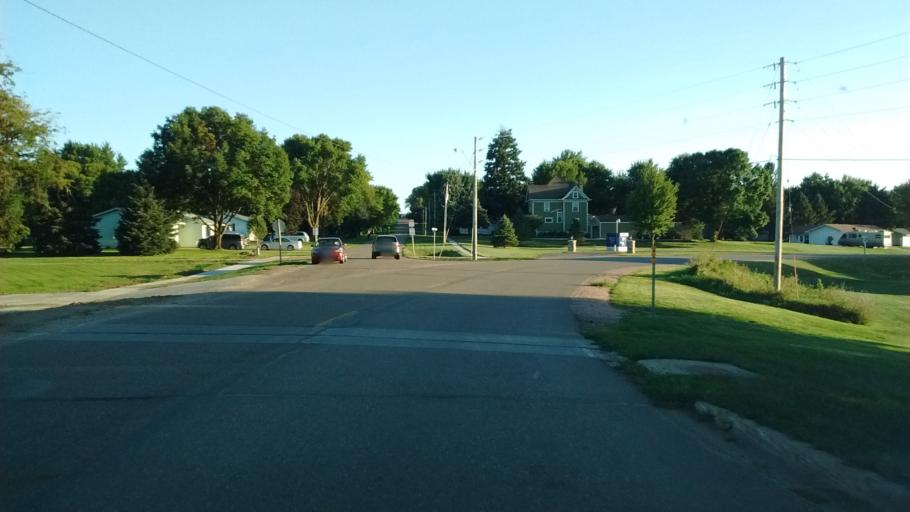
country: US
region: Iowa
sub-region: Plymouth County
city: Kingsley
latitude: 42.5853
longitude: -95.9674
